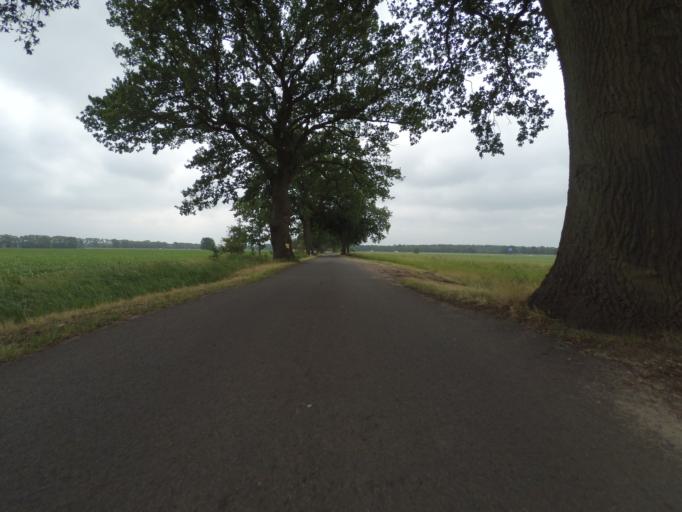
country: DE
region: Mecklenburg-Vorpommern
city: Neustadt-Glewe
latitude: 53.4197
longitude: 11.5519
